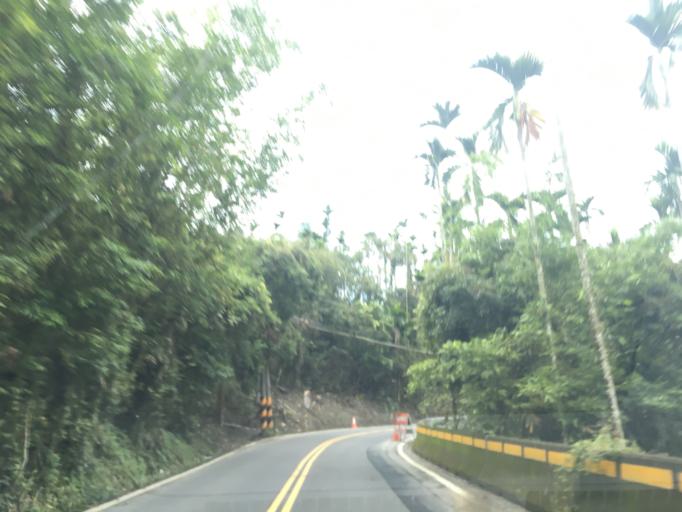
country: TW
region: Taiwan
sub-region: Yunlin
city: Douliu
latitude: 23.5701
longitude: 120.5677
